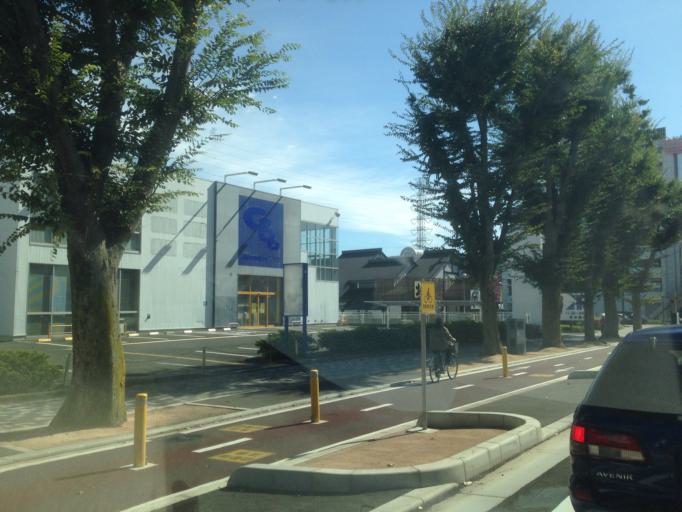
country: JP
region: Tokyo
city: Hachioji
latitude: 35.5766
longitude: 139.3665
